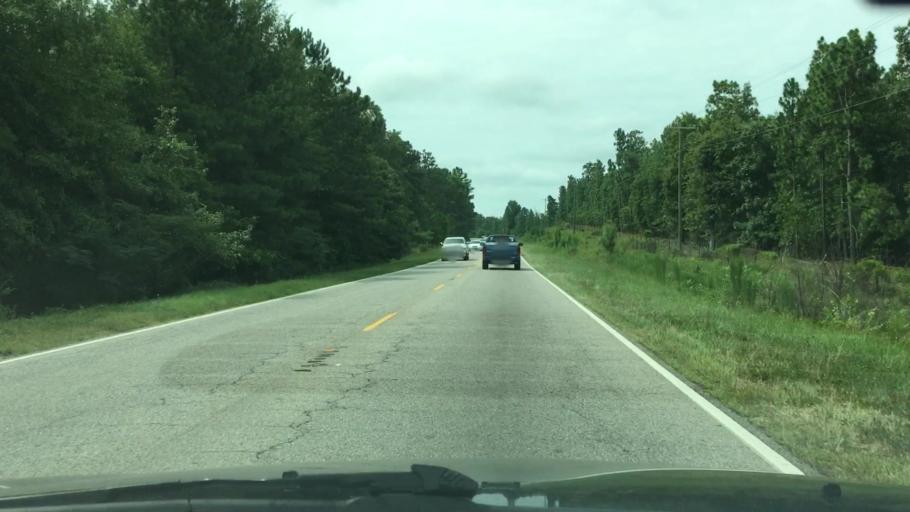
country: US
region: South Carolina
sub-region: Aiken County
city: Warrenville
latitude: 33.5402
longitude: -81.7753
